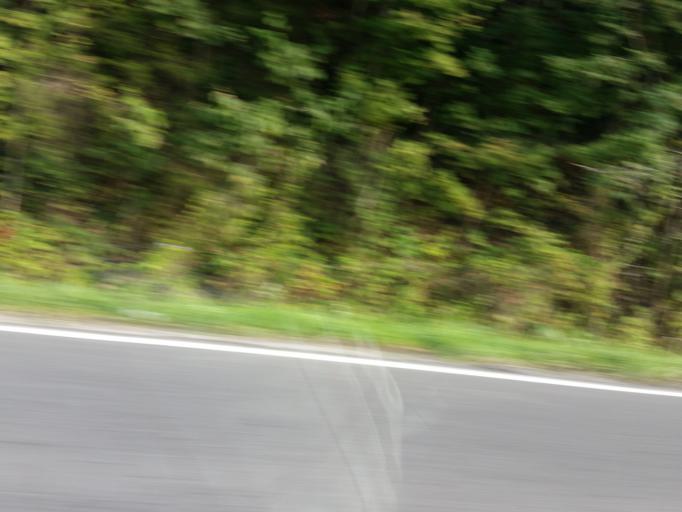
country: US
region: Tennessee
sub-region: Union County
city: Luttrell
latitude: 36.2452
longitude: -83.7478
